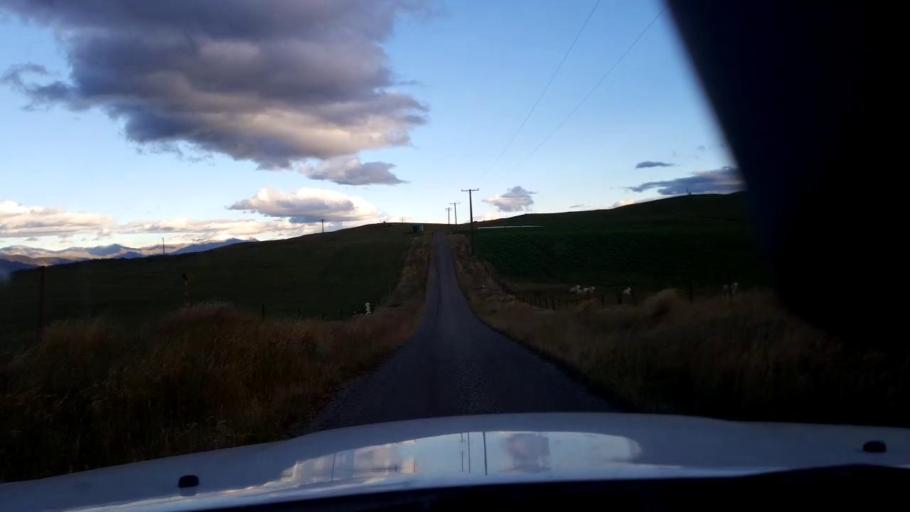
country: NZ
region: Canterbury
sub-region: Timaru District
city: Pleasant Point
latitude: -44.2483
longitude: 170.9087
